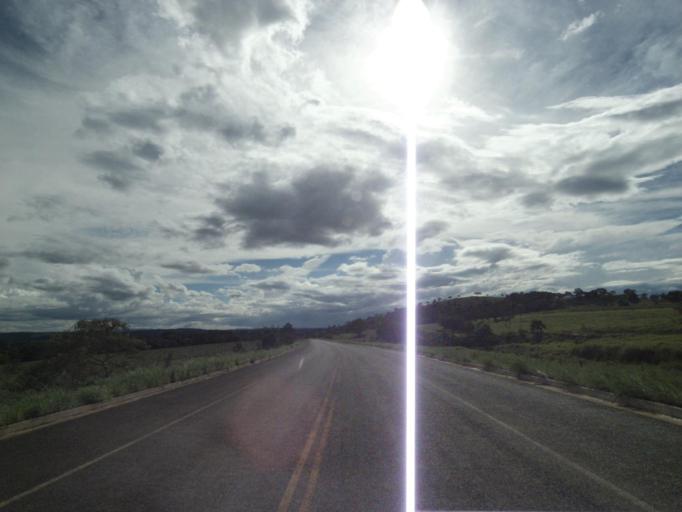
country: BR
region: Goias
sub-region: Jaragua
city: Jaragua
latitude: -15.8375
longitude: -49.3173
